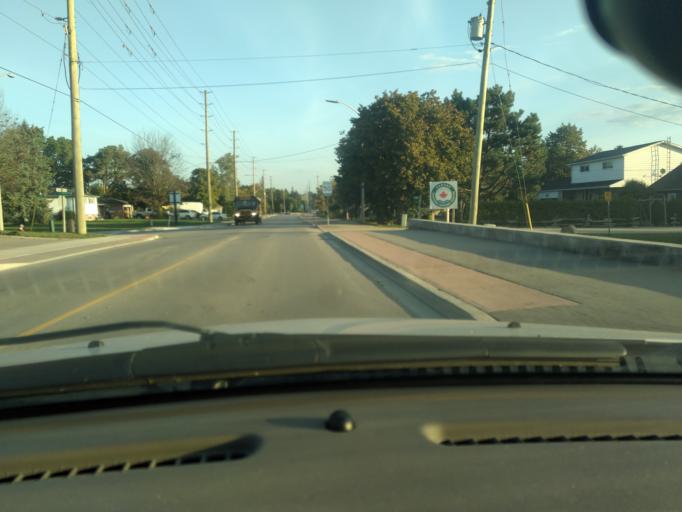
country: CA
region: Ontario
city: Bradford West Gwillimbury
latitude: 44.0918
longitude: -79.5670
